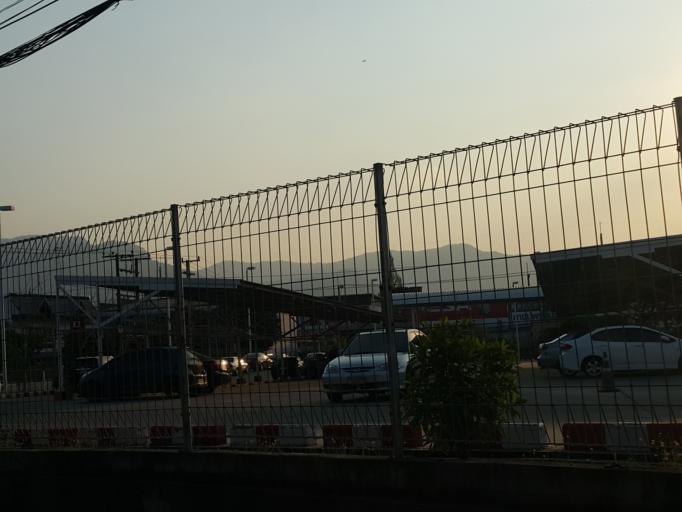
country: TH
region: Chiang Mai
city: San Sai
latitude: 18.8984
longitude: 98.9527
